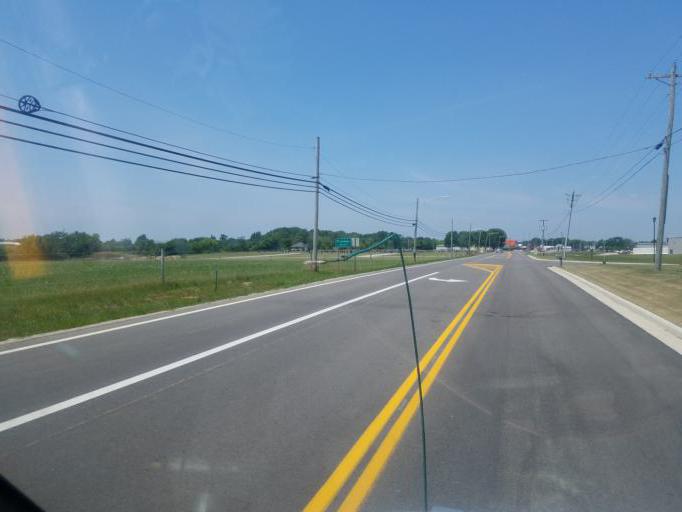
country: US
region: Ohio
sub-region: Shelby County
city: Fort Loramie
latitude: 40.3337
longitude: -84.3737
